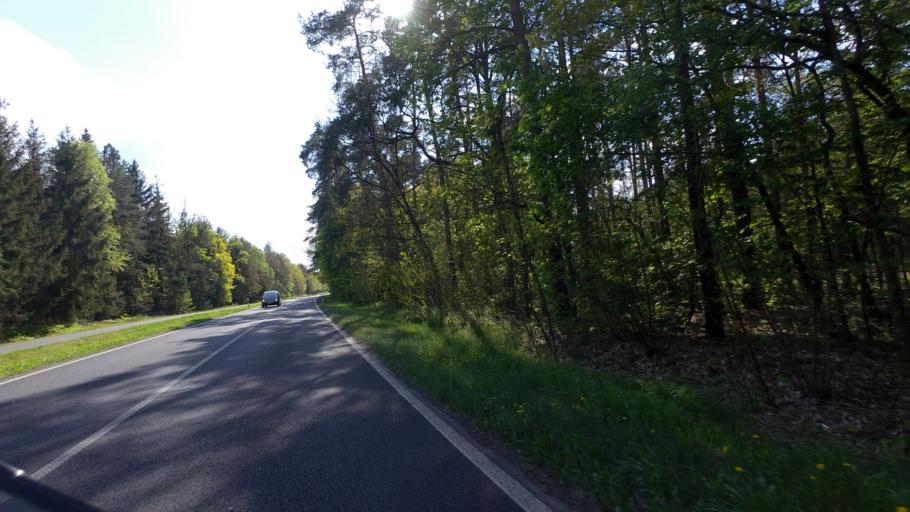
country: DE
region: Brandenburg
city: Zehdenick
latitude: 53.0096
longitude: 13.3605
